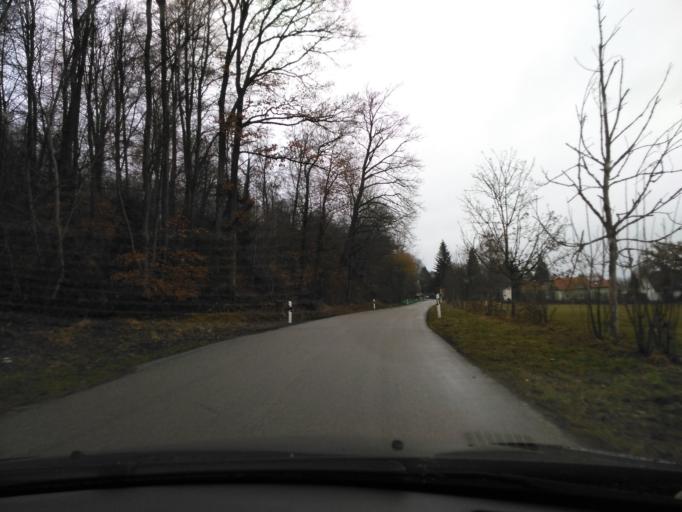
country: DE
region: Bavaria
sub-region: Upper Bavaria
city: Fuerstenfeldbruck
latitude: 48.1807
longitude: 11.2193
